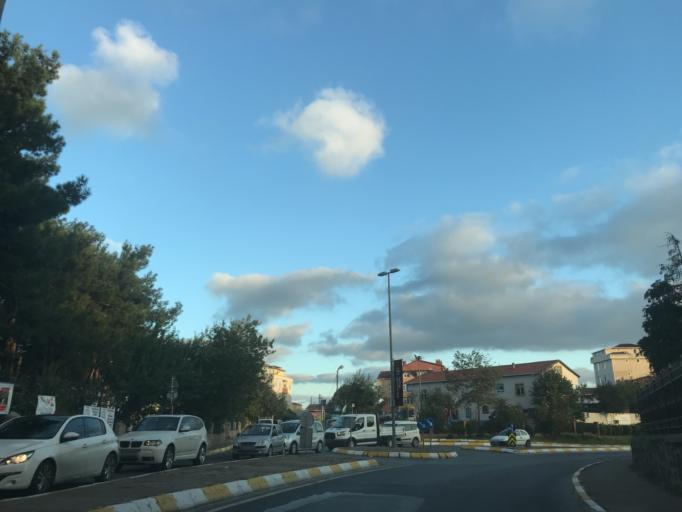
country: TR
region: Istanbul
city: Sisli
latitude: 41.1373
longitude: 29.0389
